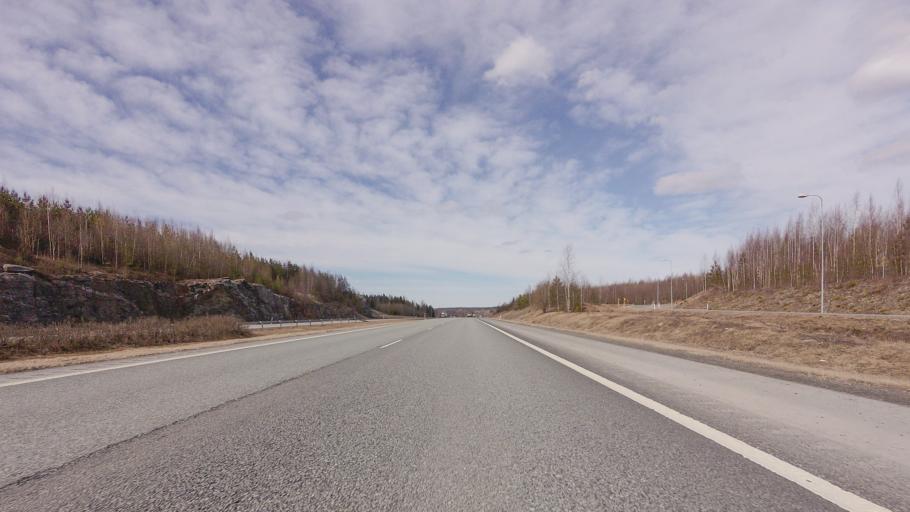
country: FI
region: Pirkanmaa
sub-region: Tampere
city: Lempaeaelae
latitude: 61.3325
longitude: 23.7980
